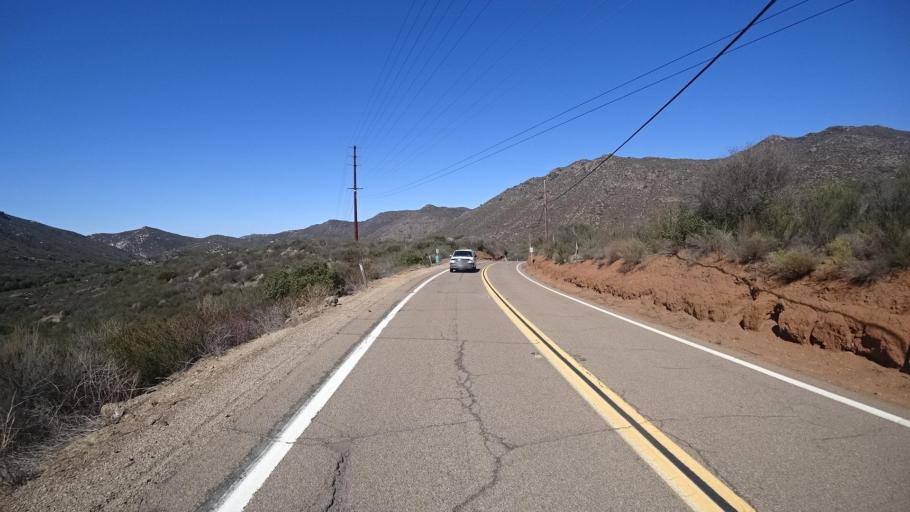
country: US
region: California
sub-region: San Diego County
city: Alpine
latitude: 32.7914
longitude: -116.7393
